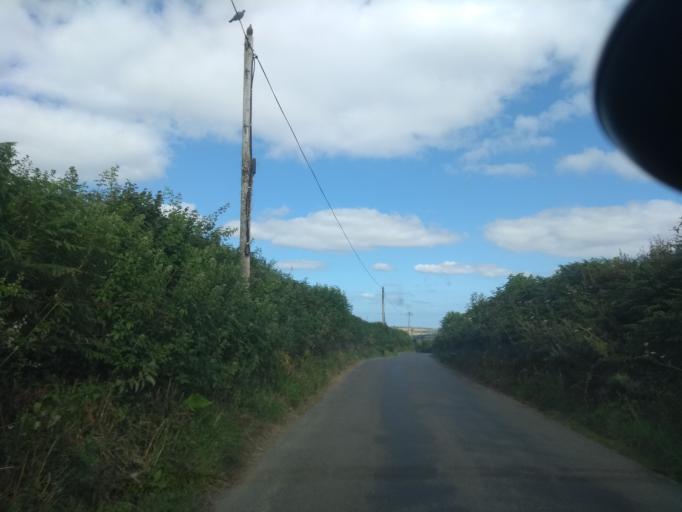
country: GB
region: England
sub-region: Devon
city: Modbury
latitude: 50.3065
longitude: -3.8656
